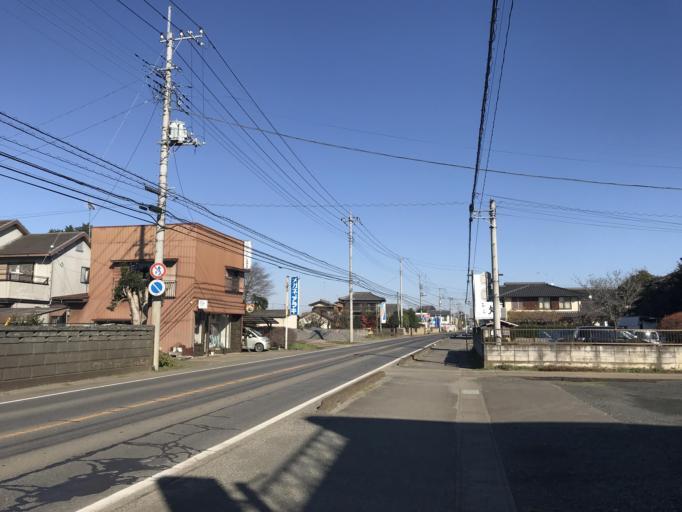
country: JP
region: Tochigi
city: Oyama
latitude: 36.2404
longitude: 139.8289
